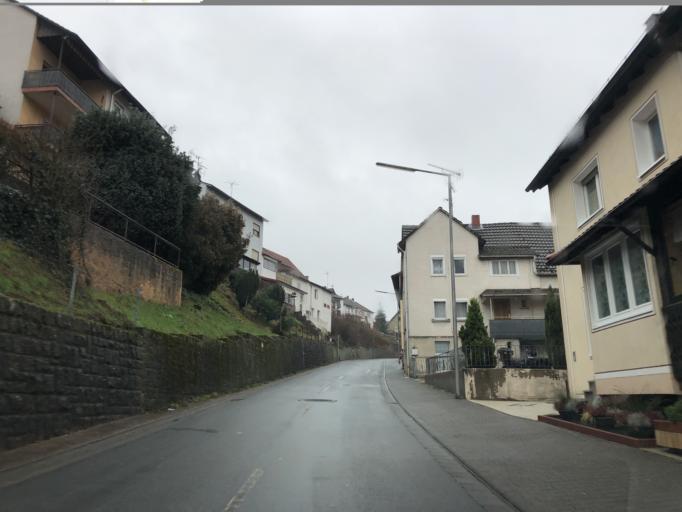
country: DE
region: Bavaria
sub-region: Regierungsbezirk Unterfranken
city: Worth am Main
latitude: 49.7850
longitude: 9.1176
